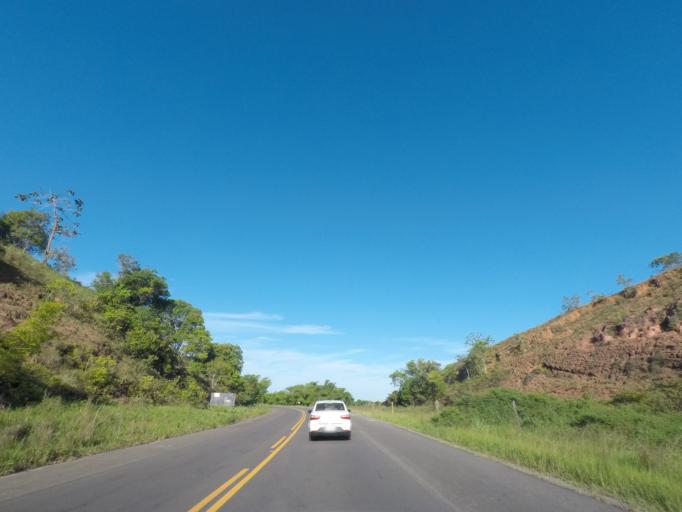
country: BR
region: Bahia
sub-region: Nazare
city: Nazare
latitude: -13.0150
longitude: -38.9773
